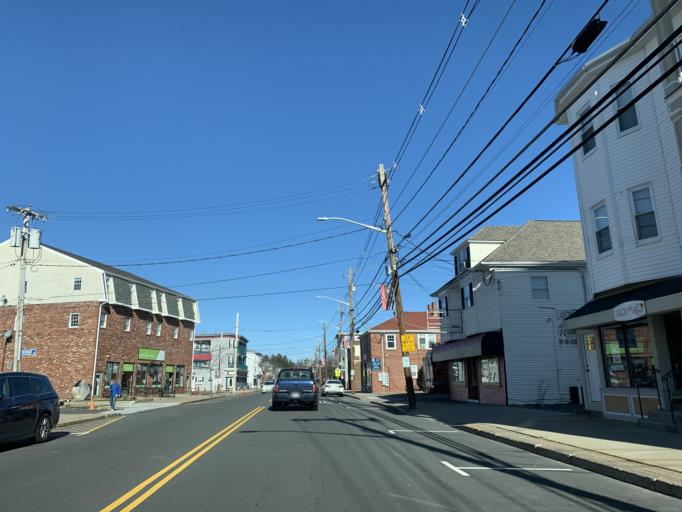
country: US
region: Massachusetts
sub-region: Norfolk County
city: Norwood
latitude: 42.1759
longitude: -71.2071
